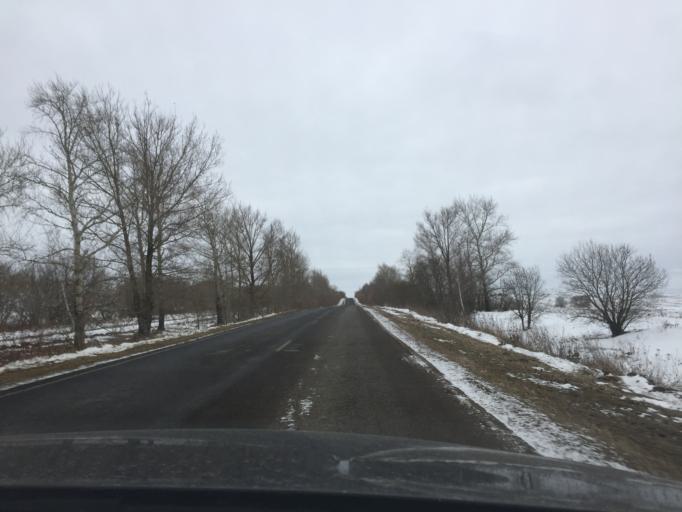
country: RU
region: Tula
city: Shchekino
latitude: 53.8241
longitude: 37.5207
